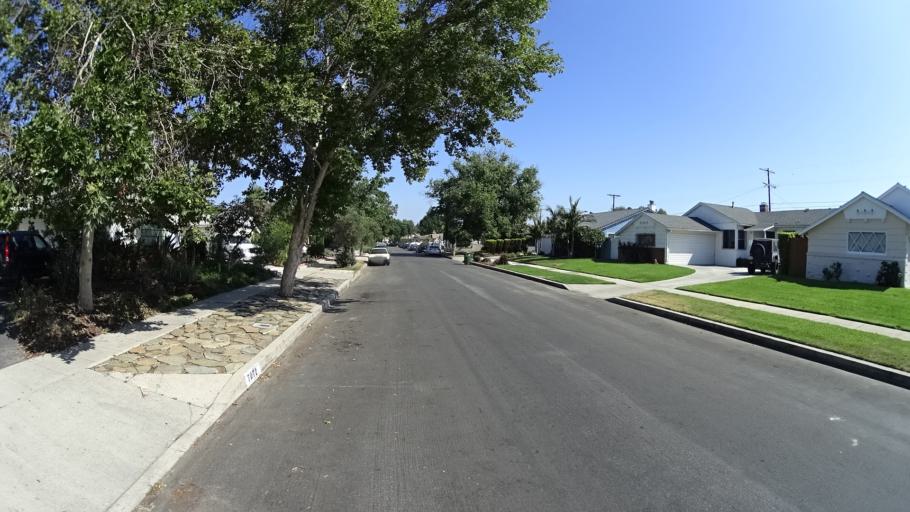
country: US
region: California
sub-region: Los Angeles County
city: Van Nuys
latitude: 34.1990
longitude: -118.4250
